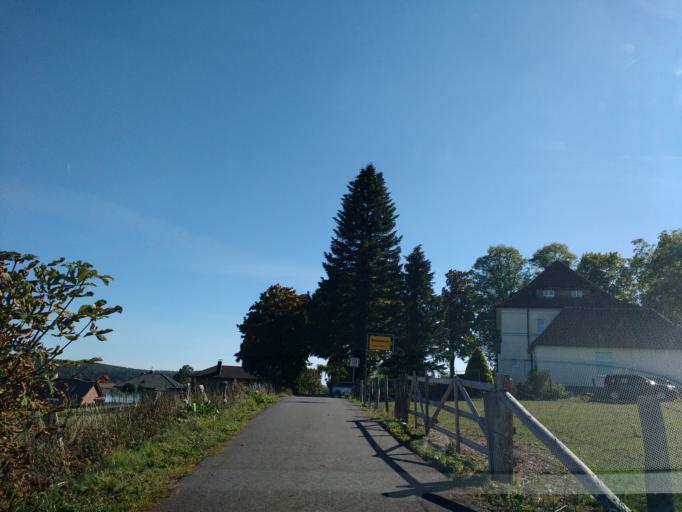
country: DE
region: North Rhine-Westphalia
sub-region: Regierungsbezirk Detmold
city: Willebadessen
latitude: 51.6249
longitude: 9.0137
